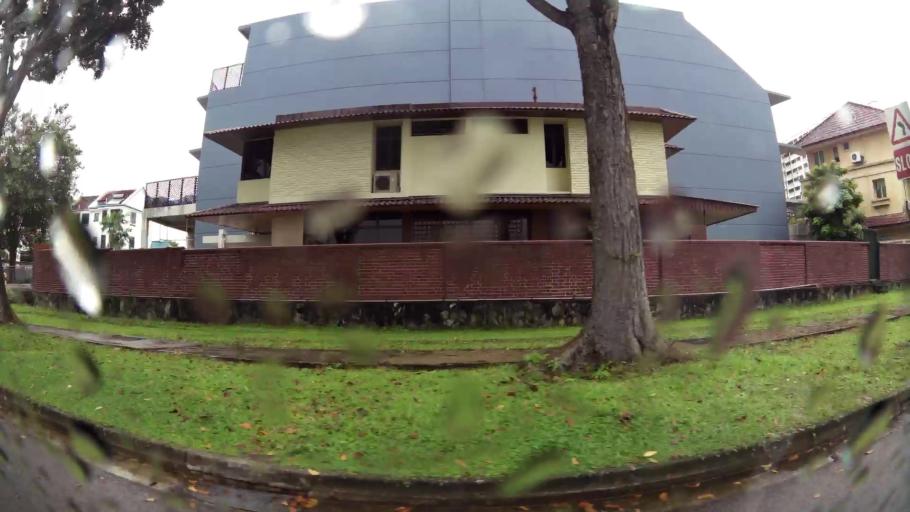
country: SG
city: Singapore
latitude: 1.3470
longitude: 103.8774
